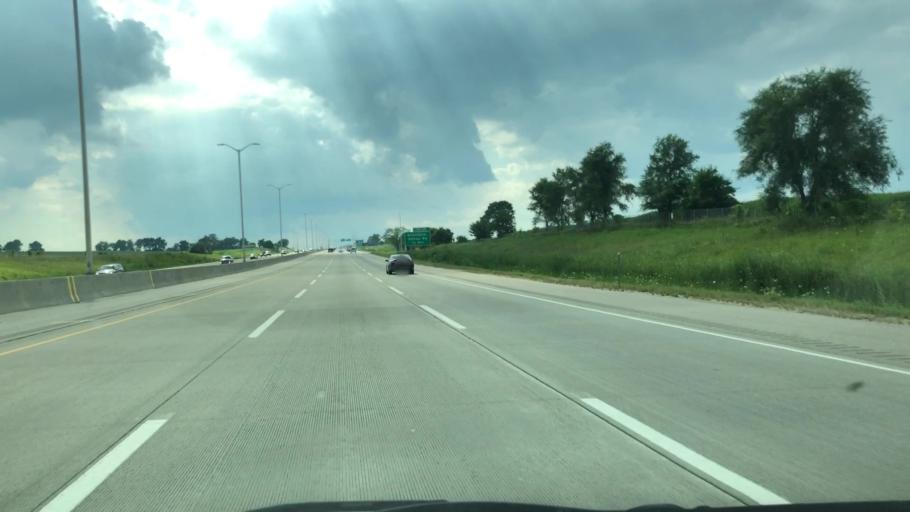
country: US
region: Illinois
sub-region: Boone County
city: Belvidere
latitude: 42.2344
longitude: -88.7986
